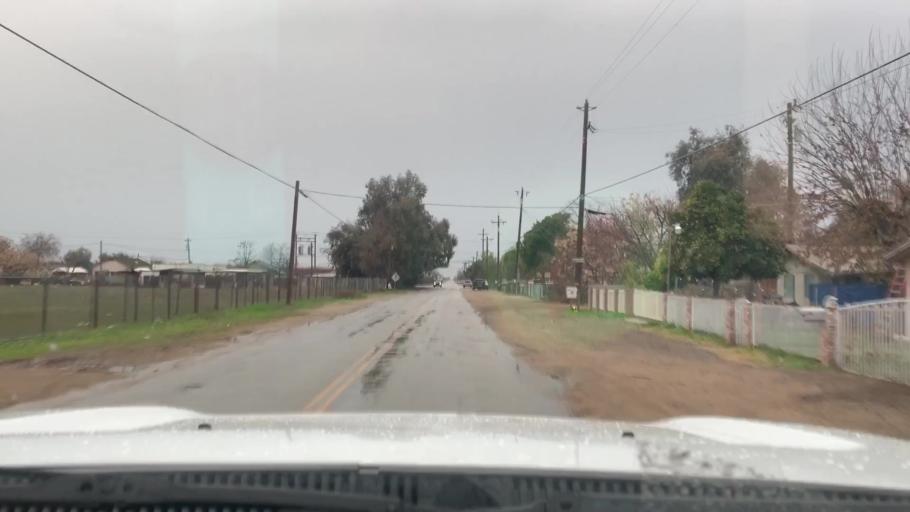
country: US
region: California
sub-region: Kern County
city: Shafter
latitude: 35.4781
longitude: -119.2766
